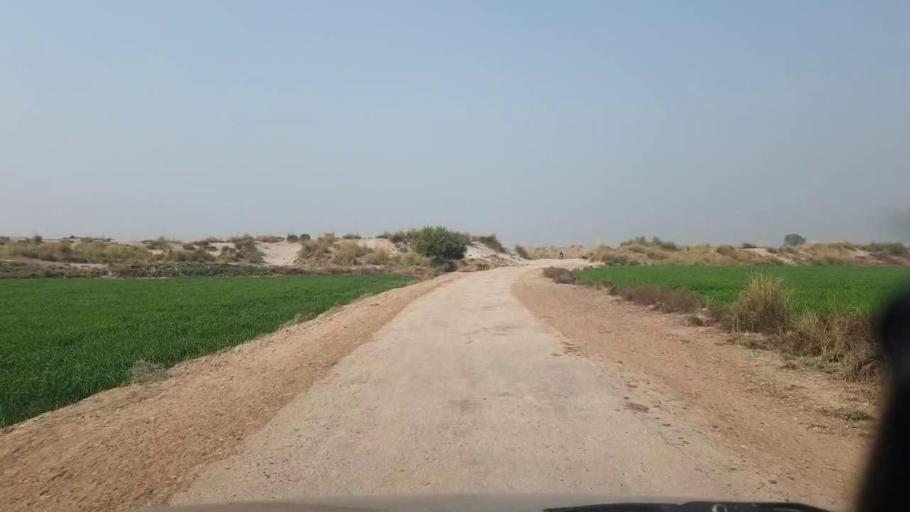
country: PK
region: Sindh
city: Shahdadpur
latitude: 26.0335
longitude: 68.5244
